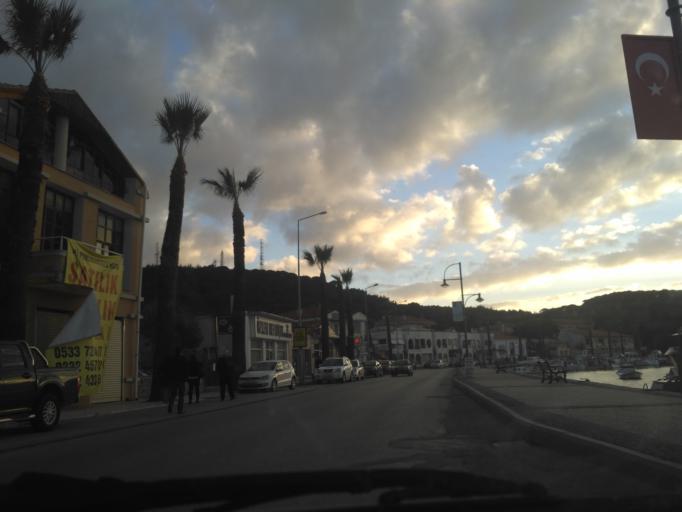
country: TR
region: Balikesir
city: Ayvalik
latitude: 39.3143
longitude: 26.6902
